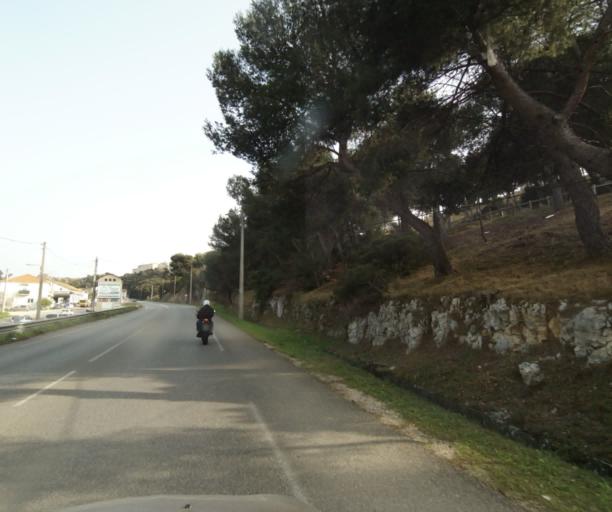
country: FR
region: Provence-Alpes-Cote d'Azur
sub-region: Departement des Bouches-du-Rhone
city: Les Pennes-Mirabeau
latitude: 43.4119
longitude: 5.3038
